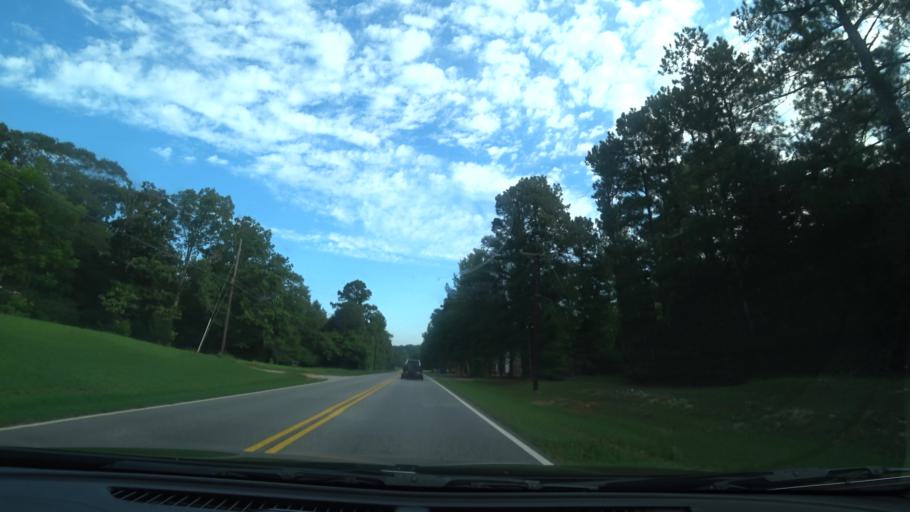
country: US
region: Georgia
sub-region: Rockdale County
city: Lakeview Estates
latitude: 33.7620
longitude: -83.9835
